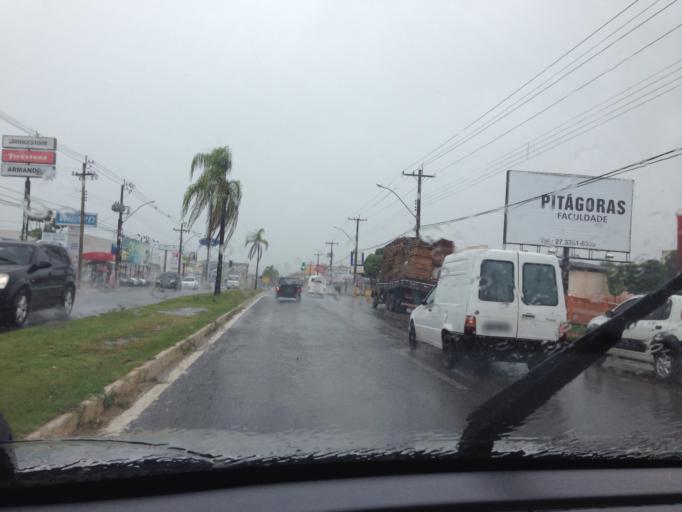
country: BR
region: Espirito Santo
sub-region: Guarapari
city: Guarapari
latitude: -20.6558
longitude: -40.5031
